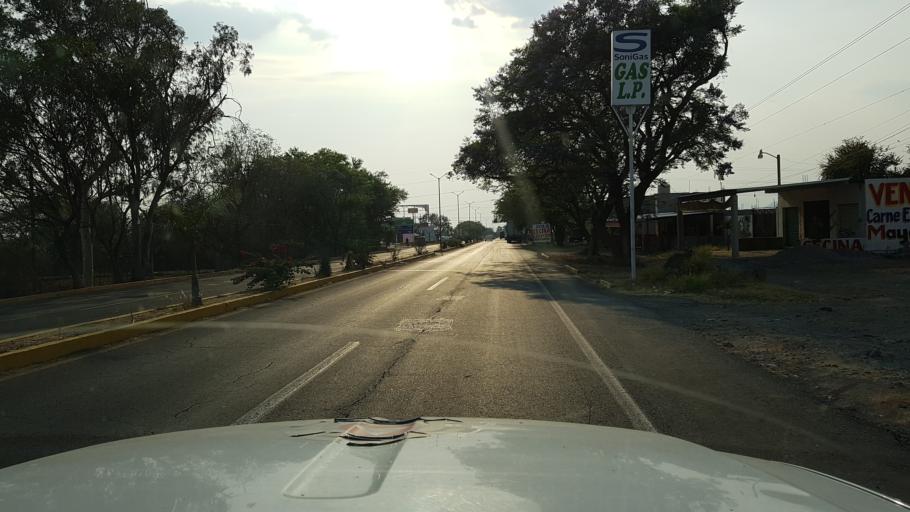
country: MX
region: Morelos
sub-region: Yecapixtla
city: Yecapixtla
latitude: 18.8897
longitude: -98.8831
